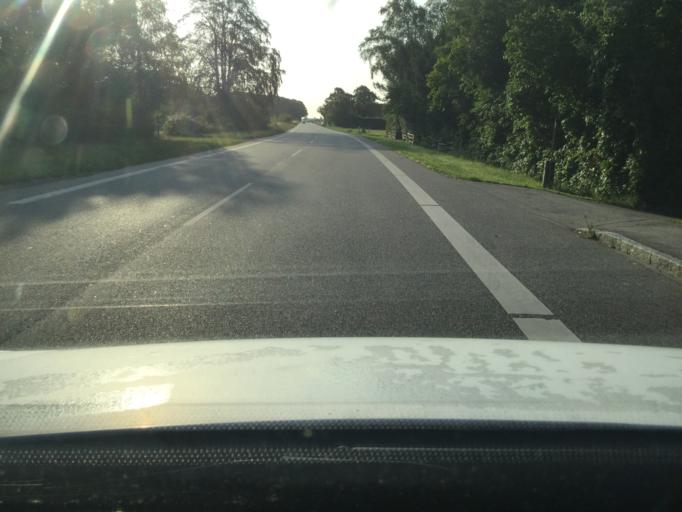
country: DK
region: Zealand
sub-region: Lolland Kommune
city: Rodby
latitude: 54.7574
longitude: 11.3420
